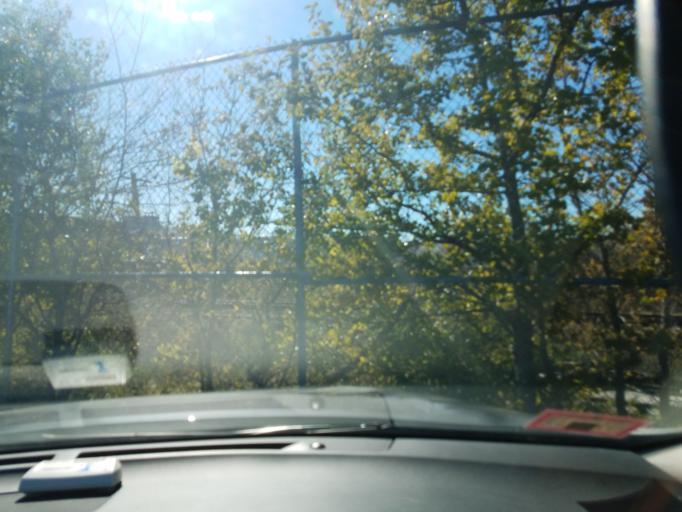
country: US
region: Illinois
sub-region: Cook County
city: Lincolnwood
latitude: 41.9598
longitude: -87.7435
